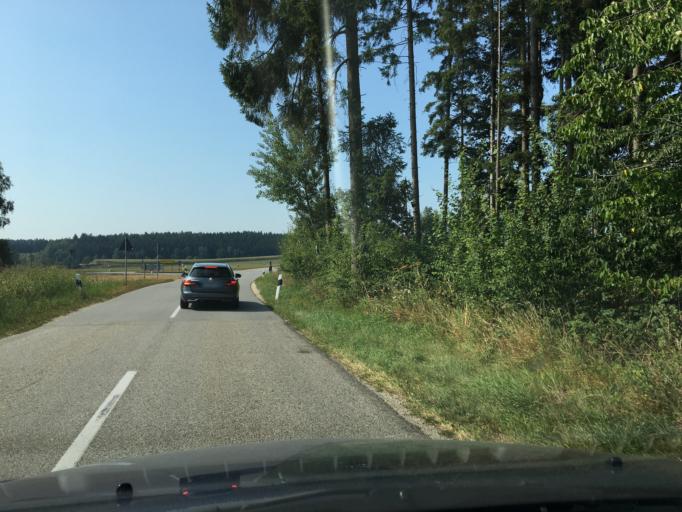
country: DE
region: Bavaria
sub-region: Upper Bavaria
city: Niederbergkirchen
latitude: 48.3293
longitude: 12.4822
